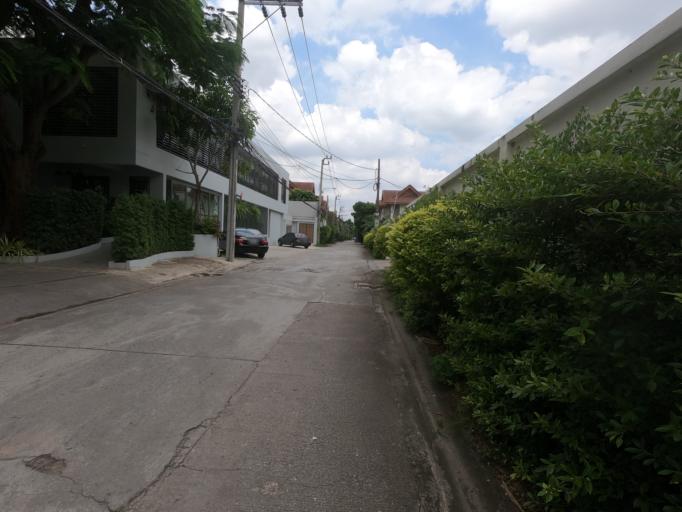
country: TH
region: Bangkok
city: Lat Phrao
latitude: 13.8231
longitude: 100.6185
